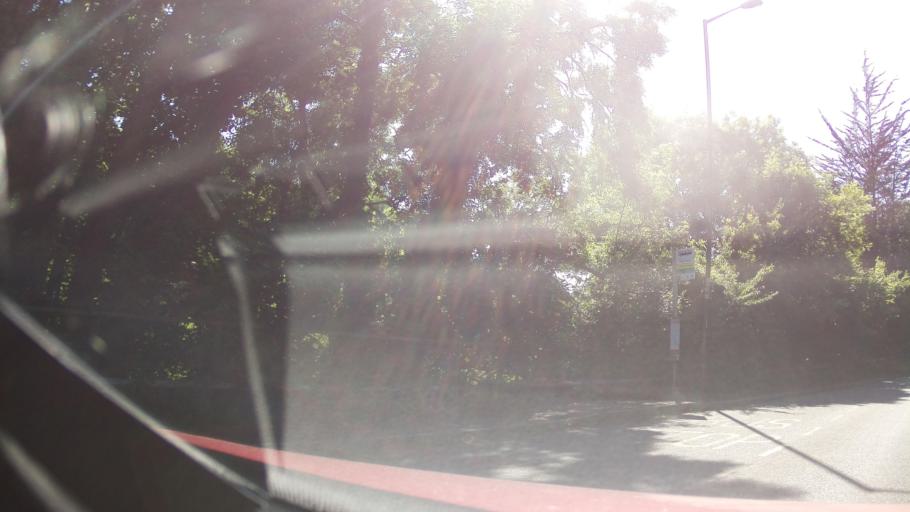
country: GB
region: England
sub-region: Borough of Torbay
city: Brixham
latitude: 50.3892
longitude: -3.5356
